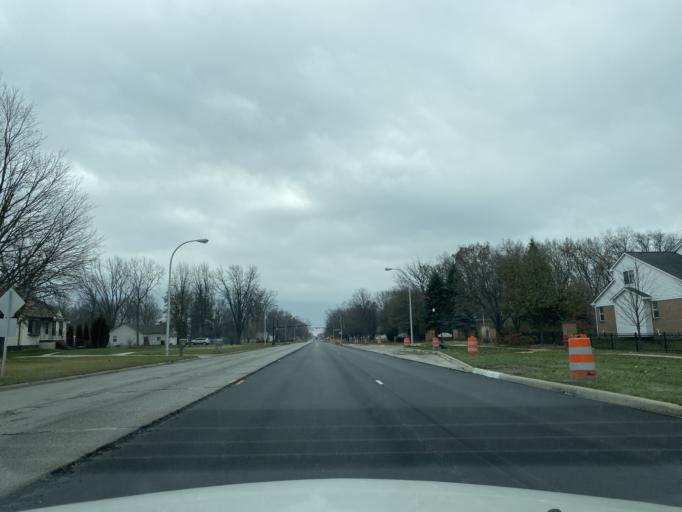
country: US
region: Michigan
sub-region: Wayne County
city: Taylor
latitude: 42.2235
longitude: -83.2882
